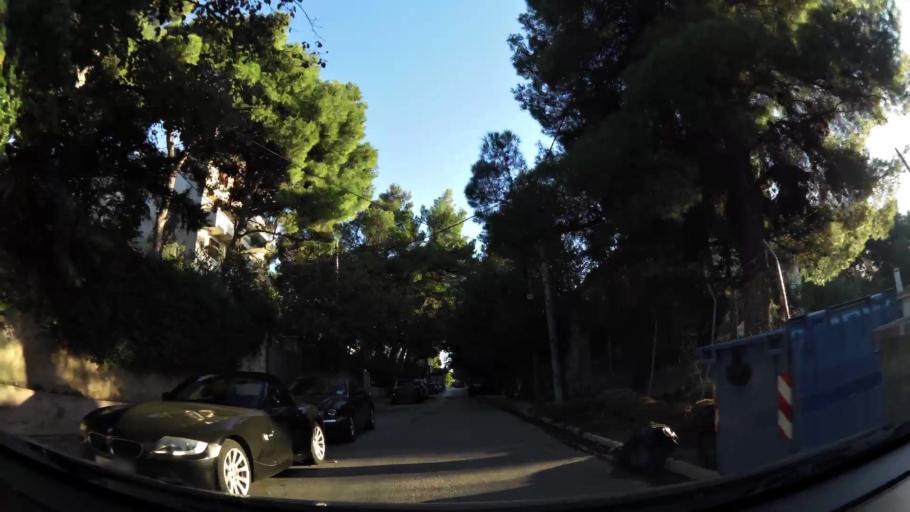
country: GR
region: Attica
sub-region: Nomarchia Athinas
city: Nea Erythraia
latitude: 38.0880
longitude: 23.8255
